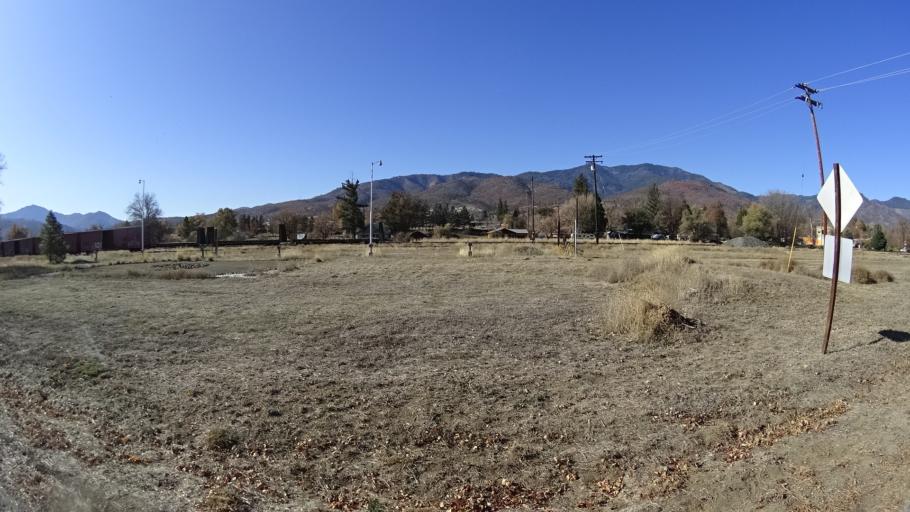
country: US
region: California
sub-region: Siskiyou County
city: Montague
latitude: 41.9094
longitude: -122.5534
